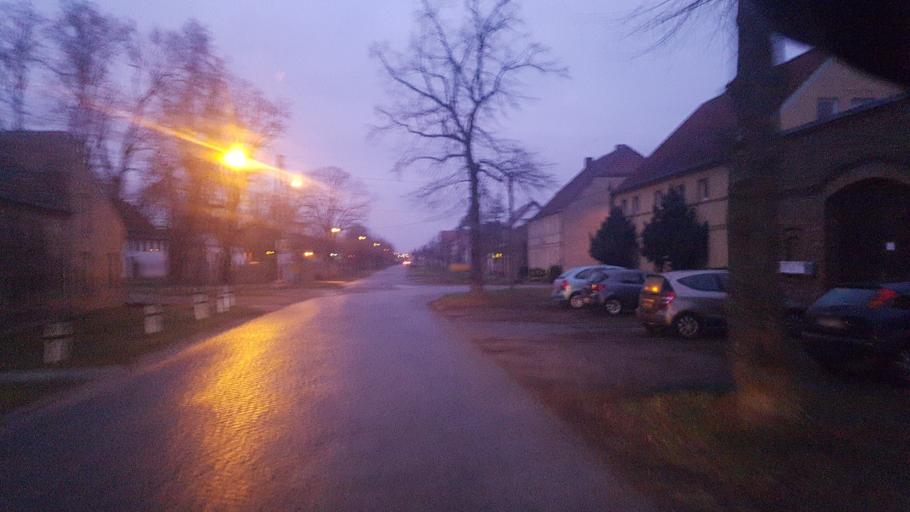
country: DE
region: Brandenburg
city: Luckenwalde
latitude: 52.1082
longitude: 13.1082
